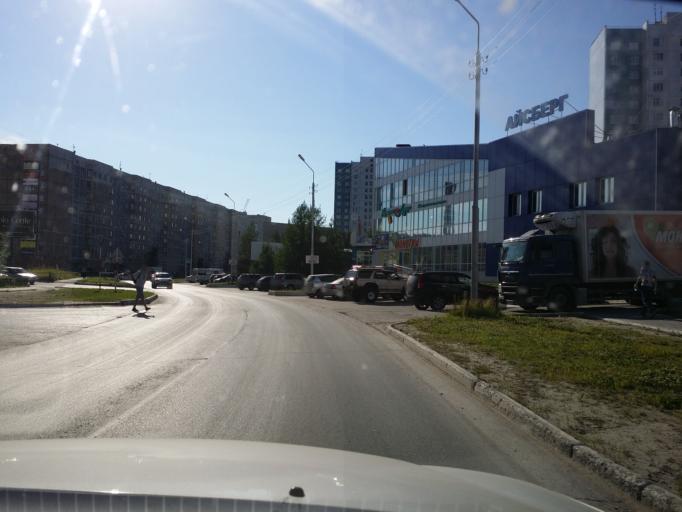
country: RU
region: Khanty-Mansiyskiy Avtonomnyy Okrug
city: Nizhnevartovsk
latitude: 60.9316
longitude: 76.5945
